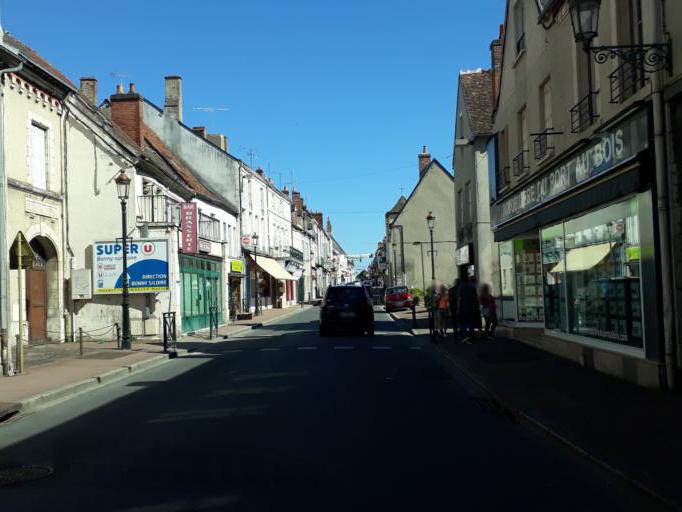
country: FR
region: Centre
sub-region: Departement du Loiret
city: Briare
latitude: 47.6397
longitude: 2.7377
